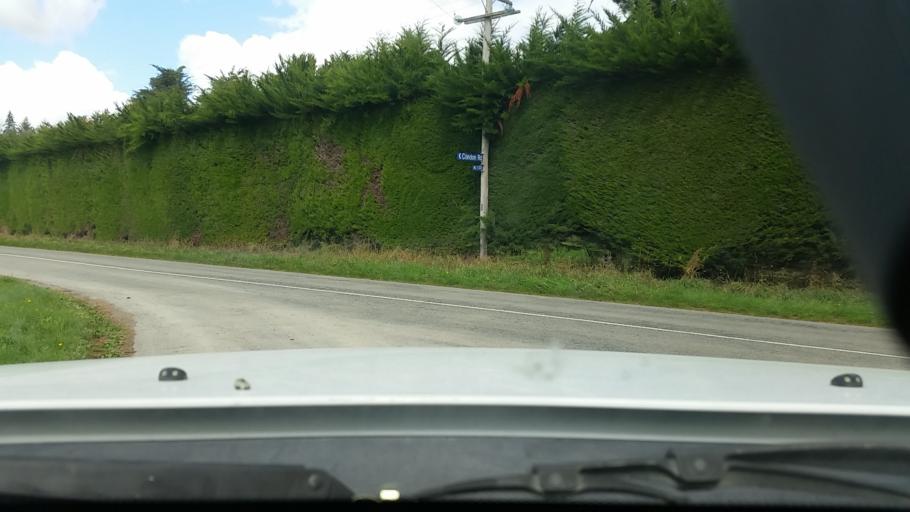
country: NZ
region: Canterbury
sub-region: Timaru District
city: Pleasant Point
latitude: -44.0232
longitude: 171.1906
